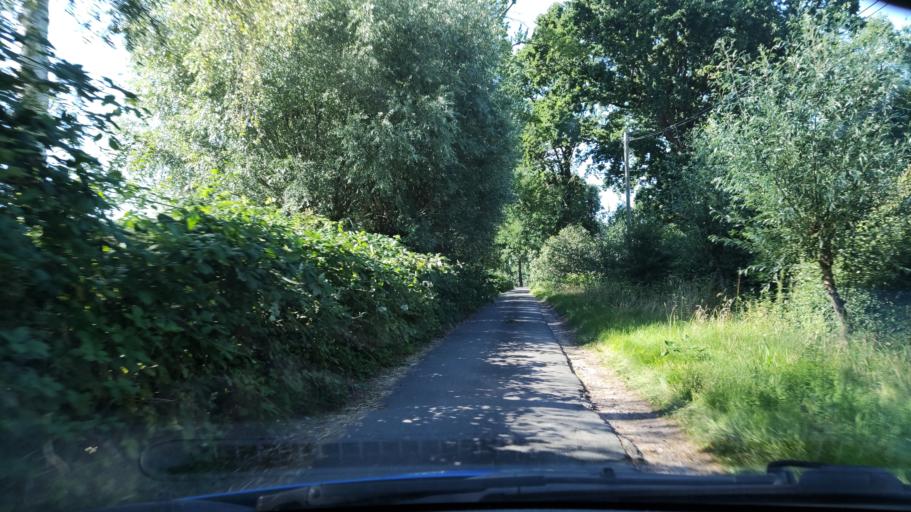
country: DE
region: Lower Saxony
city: Dahlenburg
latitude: 53.1761
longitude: 10.6880
